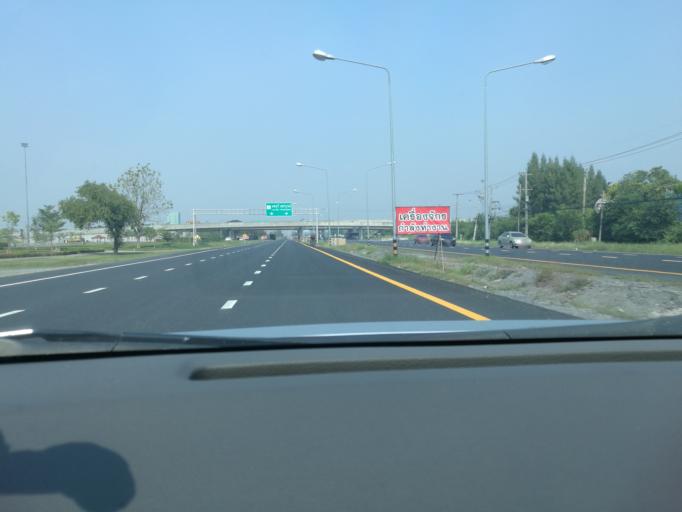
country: TH
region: Sara Buri
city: Saraburi
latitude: 14.5600
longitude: 100.9054
